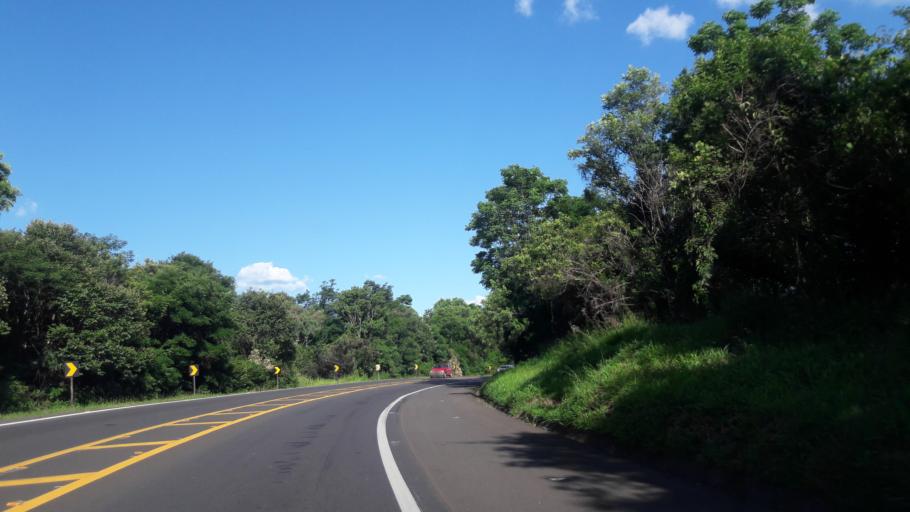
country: BR
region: Parana
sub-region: Laranjeiras Do Sul
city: Laranjeiras do Sul
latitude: -25.4189
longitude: -52.0343
